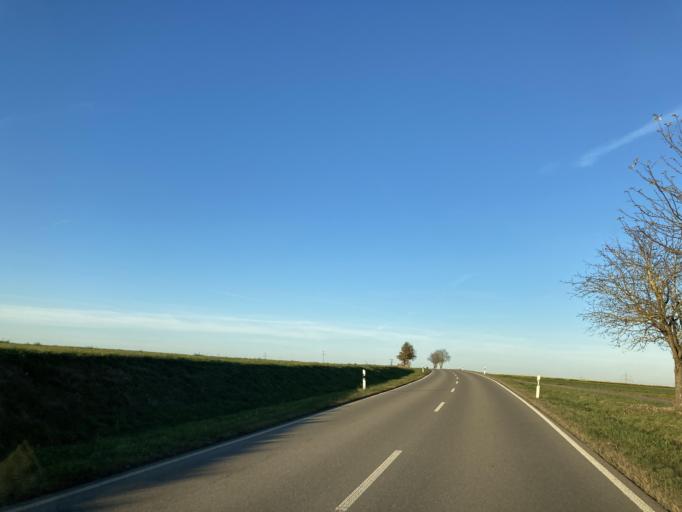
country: DE
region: Baden-Wuerttemberg
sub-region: Tuebingen Region
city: Hirrlingen
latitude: 48.4360
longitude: 8.8771
